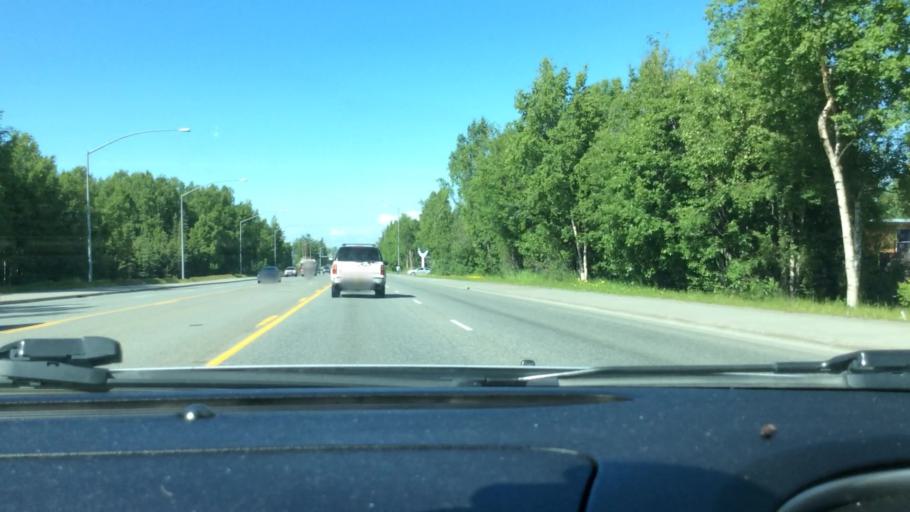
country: US
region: Alaska
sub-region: Anchorage Municipality
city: Anchorage
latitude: 61.2138
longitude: -149.7784
